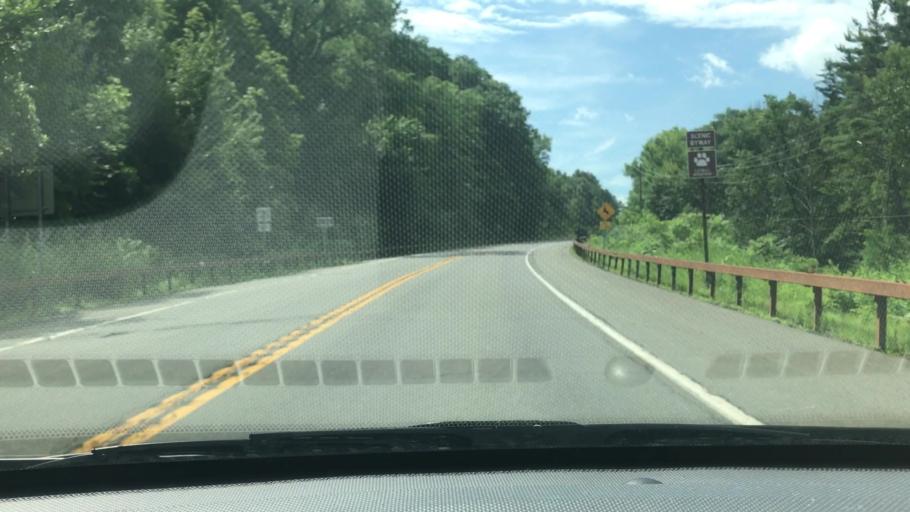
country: US
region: New York
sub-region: Ulster County
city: Shokan
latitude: 42.0039
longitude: -74.2654
